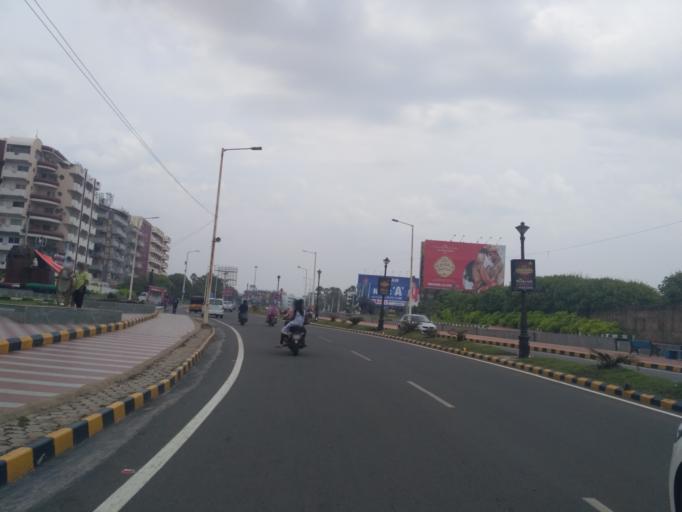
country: IN
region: Andhra Pradesh
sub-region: Vishakhapatnam
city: Yarada
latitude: 17.7196
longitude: 83.3342
